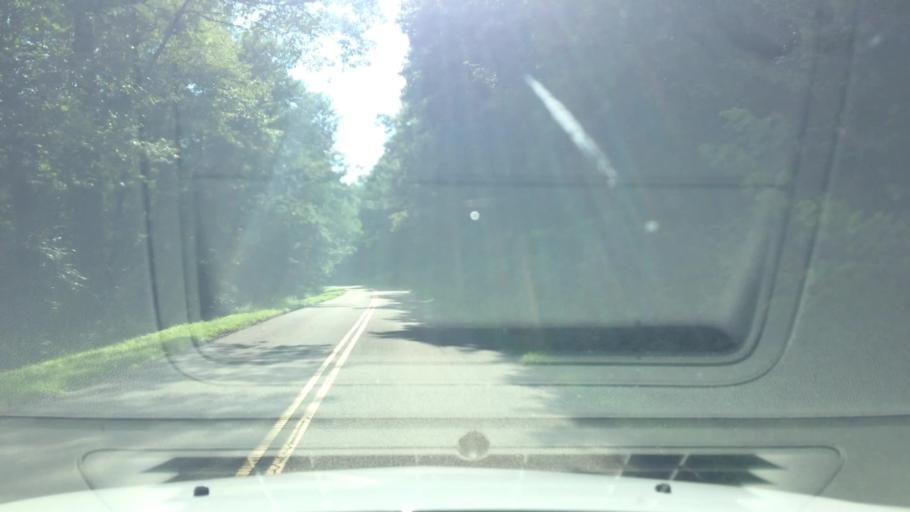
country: US
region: North Carolina
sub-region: Watauga County
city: Blowing Rock
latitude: 36.1523
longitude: -81.6858
